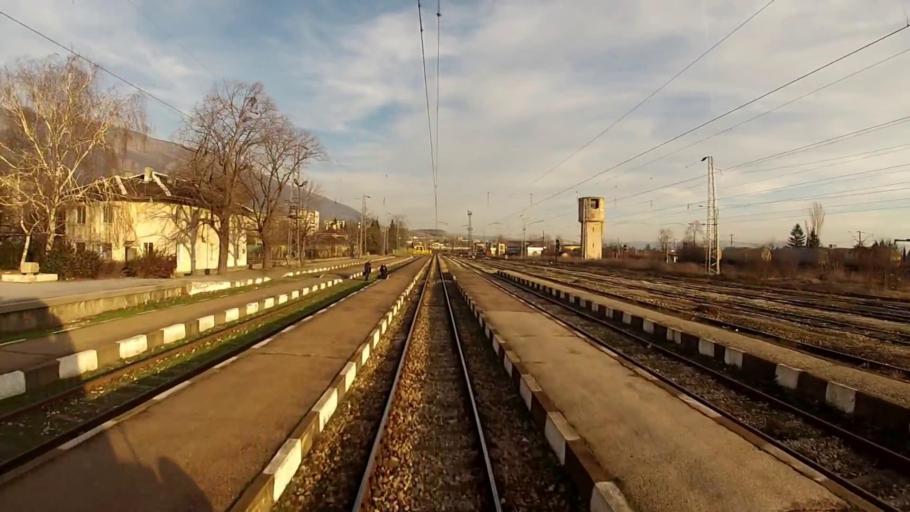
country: BG
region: Plovdiv
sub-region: Obshtina Karlovo
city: Karlovo
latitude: 42.6316
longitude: 24.8020
